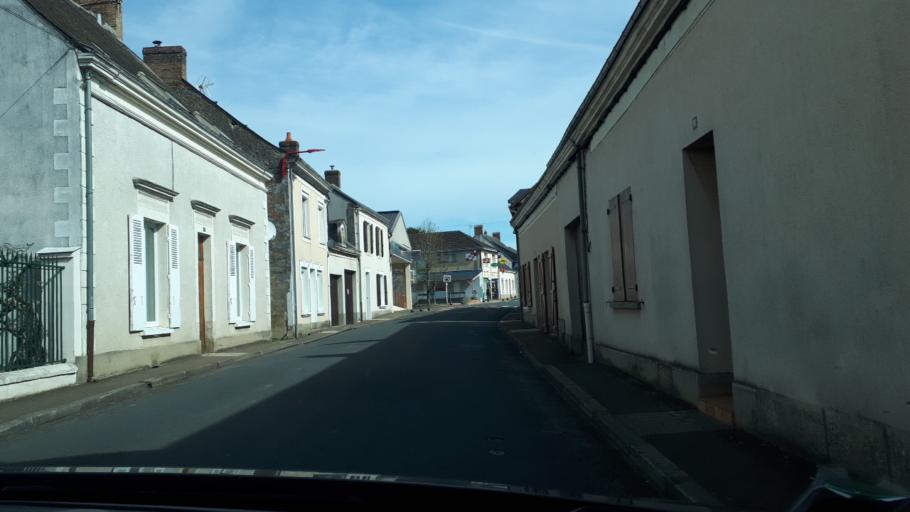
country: FR
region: Pays de la Loire
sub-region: Departement de la Sarthe
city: Yvre-le-Polin
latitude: 47.8191
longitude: 0.1531
